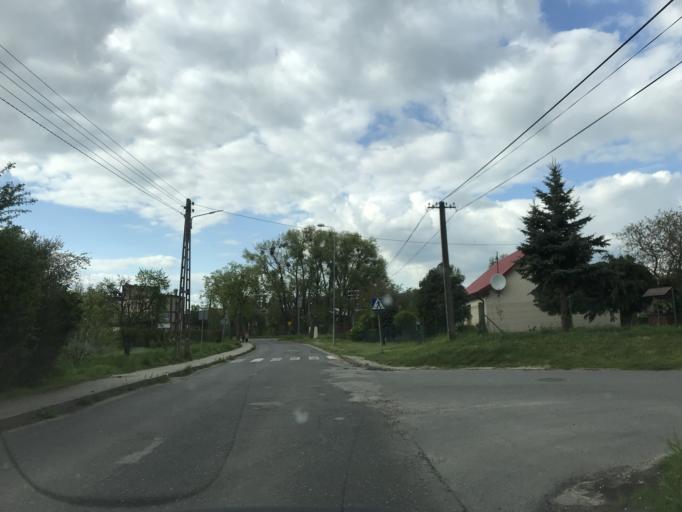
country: PL
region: West Pomeranian Voivodeship
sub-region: Powiat mysliborski
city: Mysliborz
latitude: 52.9210
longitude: 14.8836
